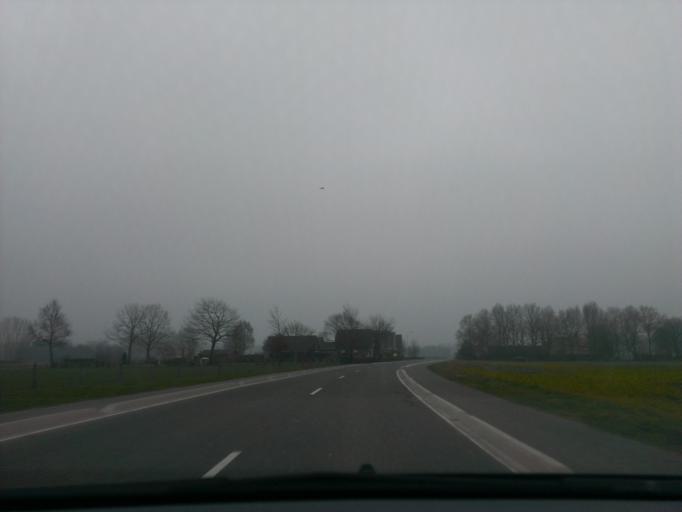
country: NL
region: Gelderland
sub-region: Gemeente Voorst
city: Twello
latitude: 52.2577
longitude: 6.1101
